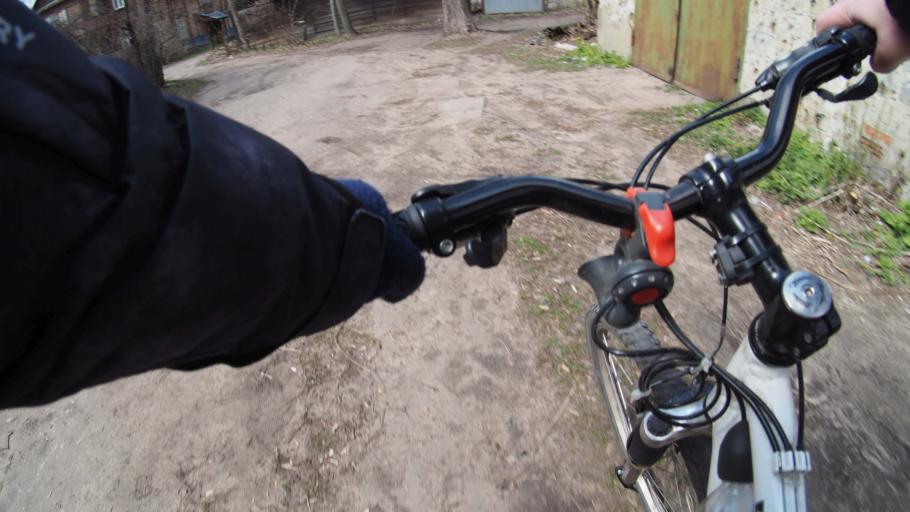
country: RU
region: Moskovskaya
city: Ramenskoye
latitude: 55.5602
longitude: 38.2447
